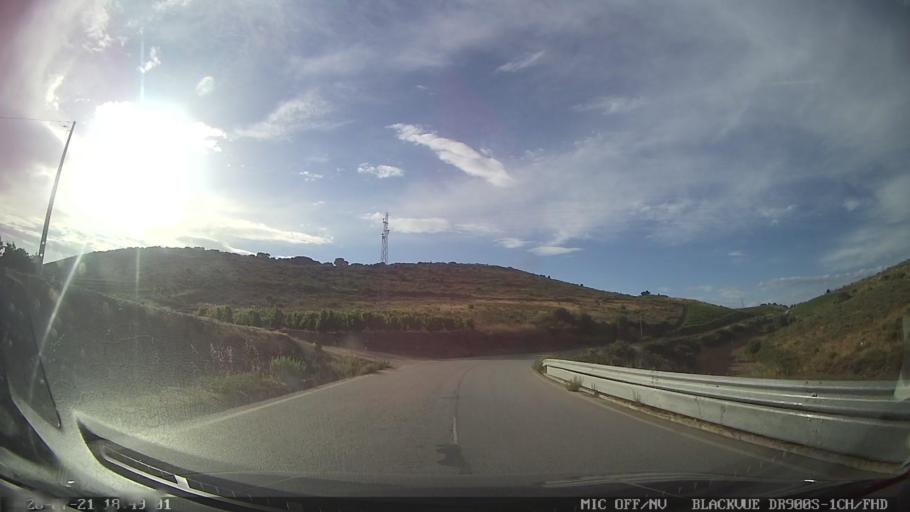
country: PT
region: Viseu
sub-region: Sao Joao da Pesqueira
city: Sao Joao da Pesqueira
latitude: 41.1321
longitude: -7.4384
